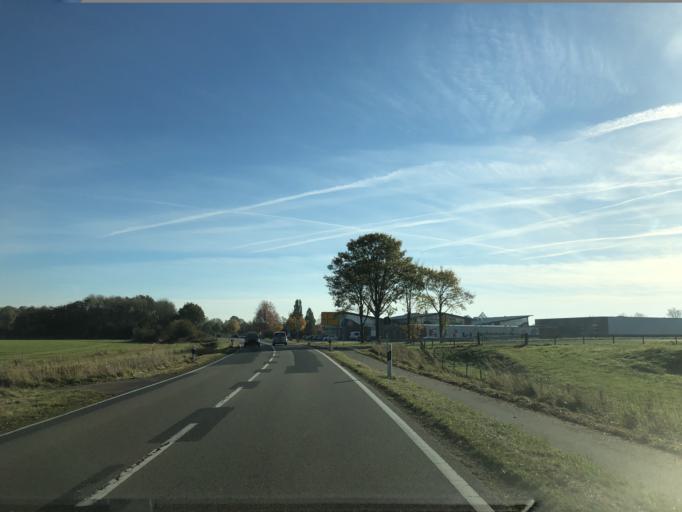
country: DE
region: Lower Saxony
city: Rhede
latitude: 53.0514
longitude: 7.3188
